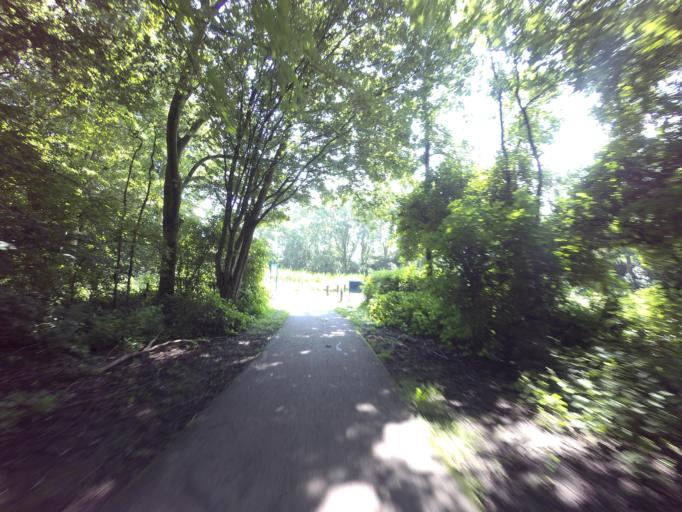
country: NL
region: North Holland
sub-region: Gemeente Enkhuizen
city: Enkhuizen
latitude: 52.7095
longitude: 5.2569
